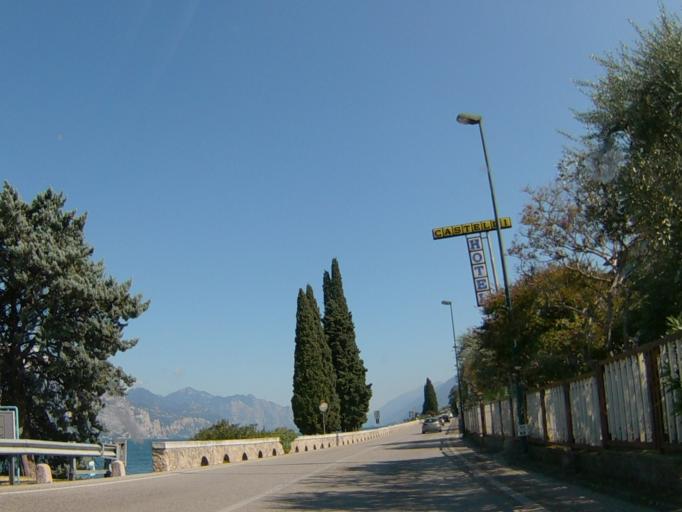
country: IT
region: Veneto
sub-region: Provincia di Verona
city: San Zeno di Montagna
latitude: 45.6682
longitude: 10.7328
